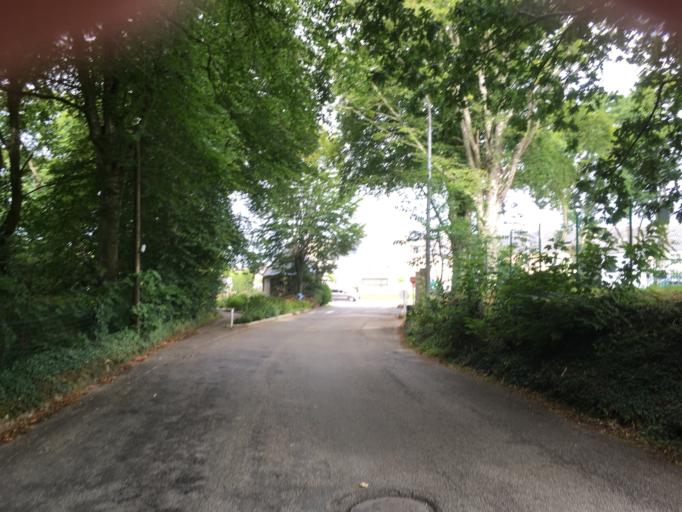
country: FR
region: Brittany
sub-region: Departement du Finistere
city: Douarnenez
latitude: 48.0856
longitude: -4.3103
